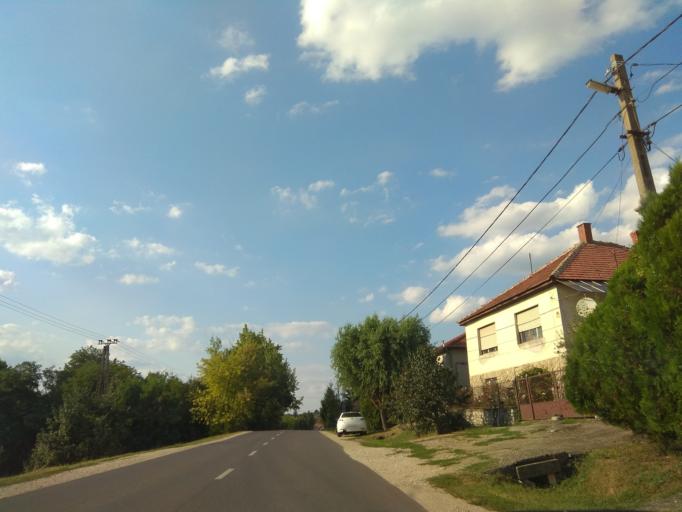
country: HU
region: Borsod-Abauj-Zemplen
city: Harsany
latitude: 47.9578
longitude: 20.7439
